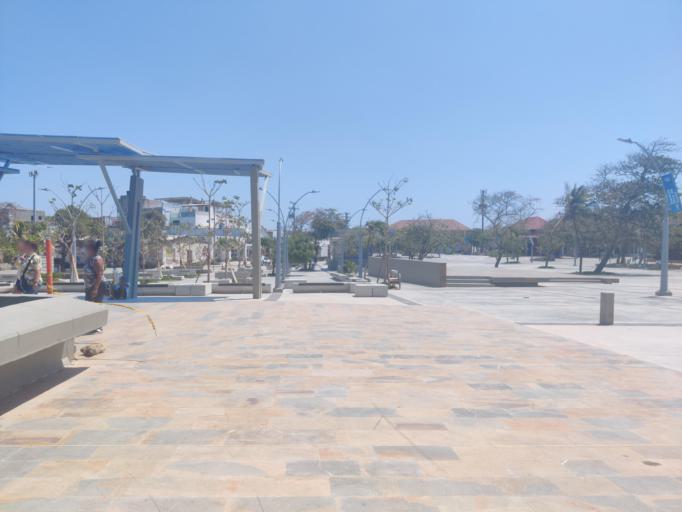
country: CO
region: Atlantico
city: Puerto Colombia
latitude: 10.9892
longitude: -74.9599
